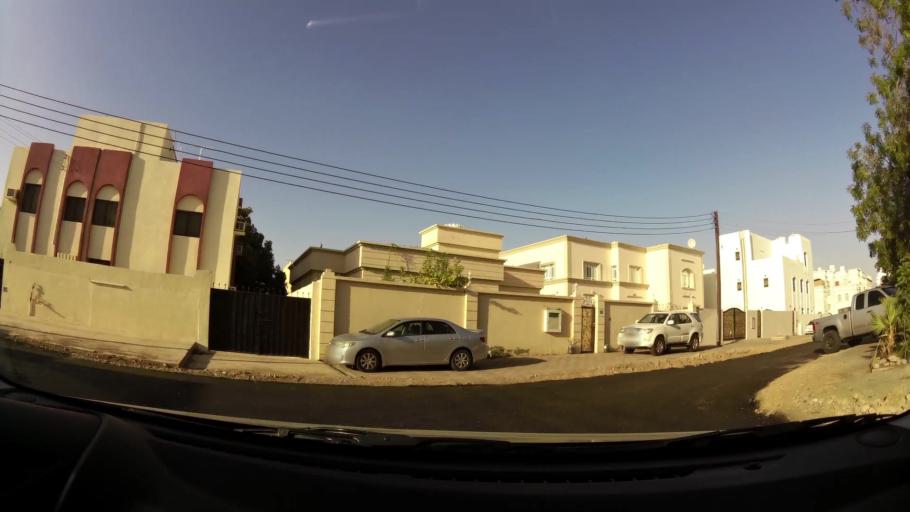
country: OM
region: Muhafazat Masqat
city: As Sib al Jadidah
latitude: 23.6310
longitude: 58.1928
